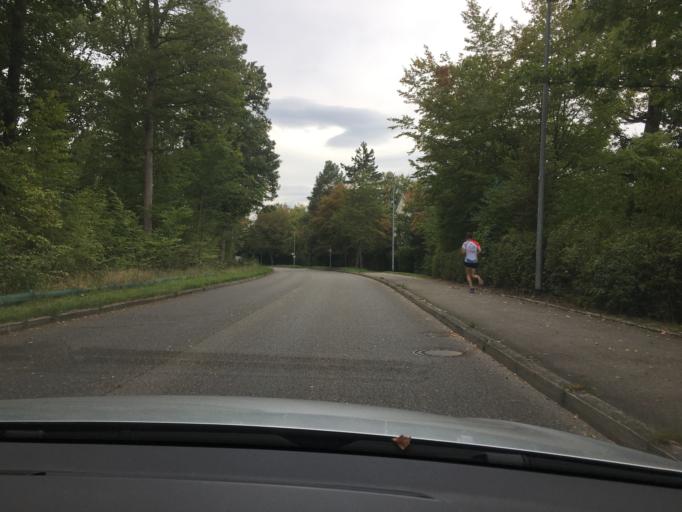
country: DE
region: Baden-Wuerttemberg
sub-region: Regierungsbezirk Stuttgart
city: Boeblingen
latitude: 48.6679
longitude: 8.9982
